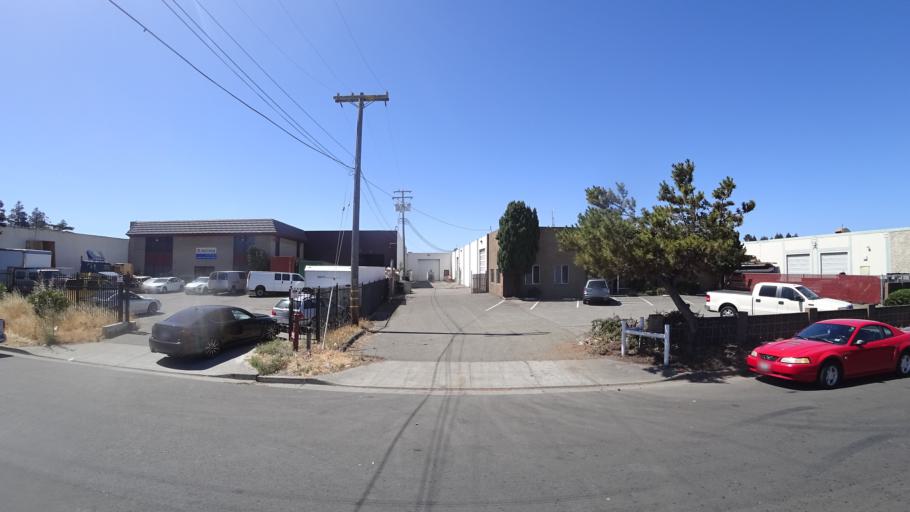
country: US
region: California
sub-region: Alameda County
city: San Lorenzo
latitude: 37.6496
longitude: -122.1224
